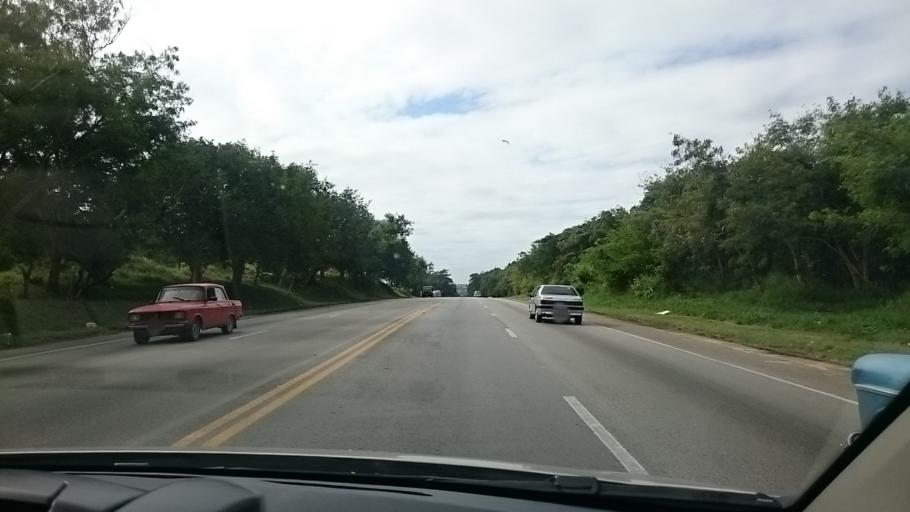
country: CU
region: La Habana
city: Alamar
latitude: 23.1532
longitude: -82.2738
